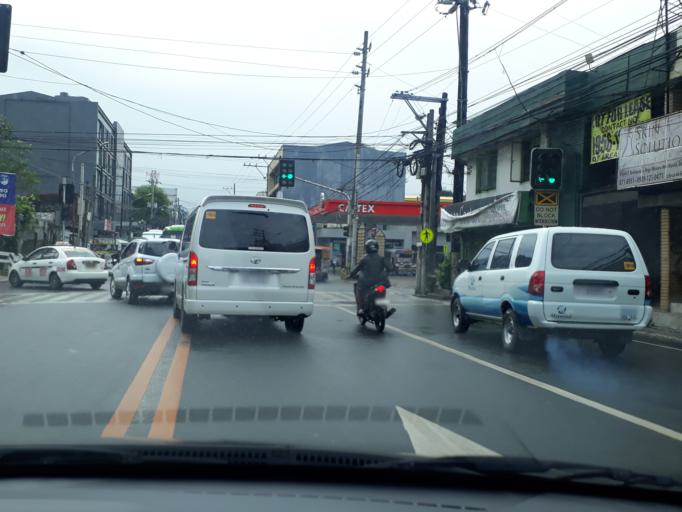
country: PH
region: Metro Manila
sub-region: San Juan
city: San Juan
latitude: 14.6244
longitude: 121.0371
